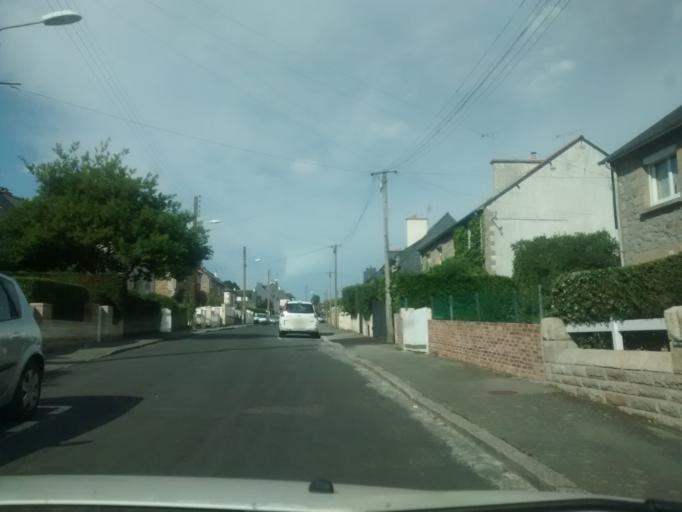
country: FR
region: Brittany
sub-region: Departement d'Ille-et-Vilaine
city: Saint-Malo
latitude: 48.6662
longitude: -1.9854
